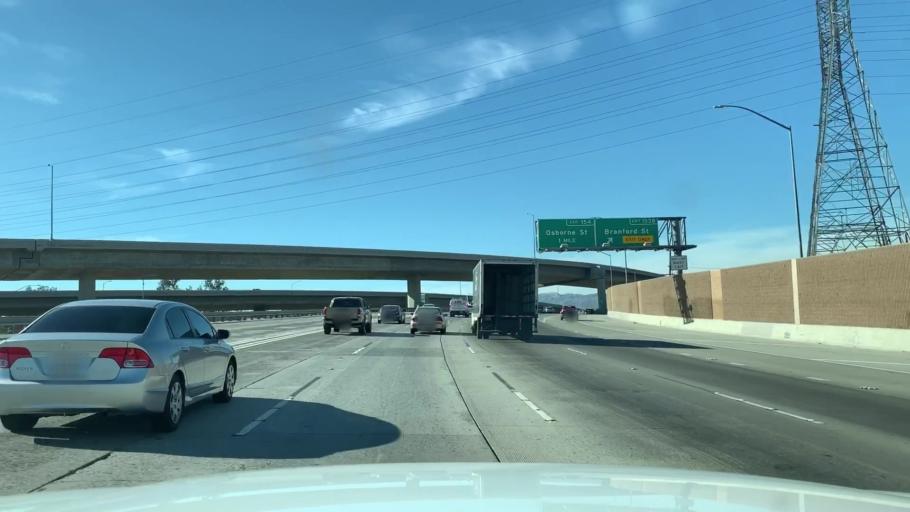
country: US
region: California
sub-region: Los Angeles County
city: San Fernando
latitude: 34.2324
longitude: -118.4078
